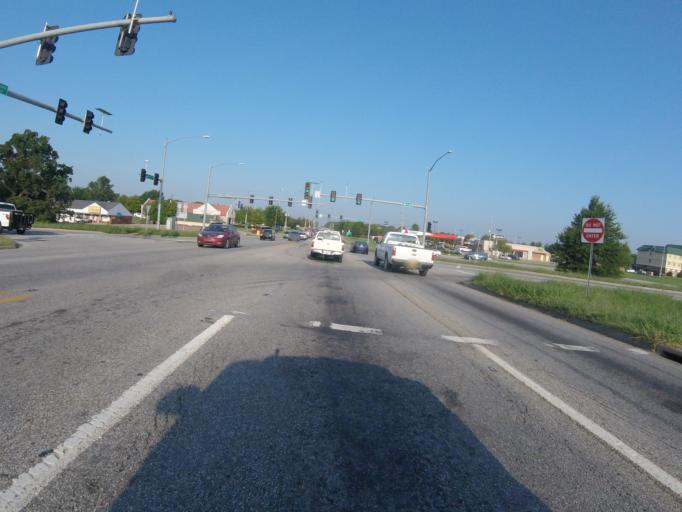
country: US
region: Arkansas
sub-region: Washington County
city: Fayetteville
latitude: 36.0783
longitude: -94.2020
